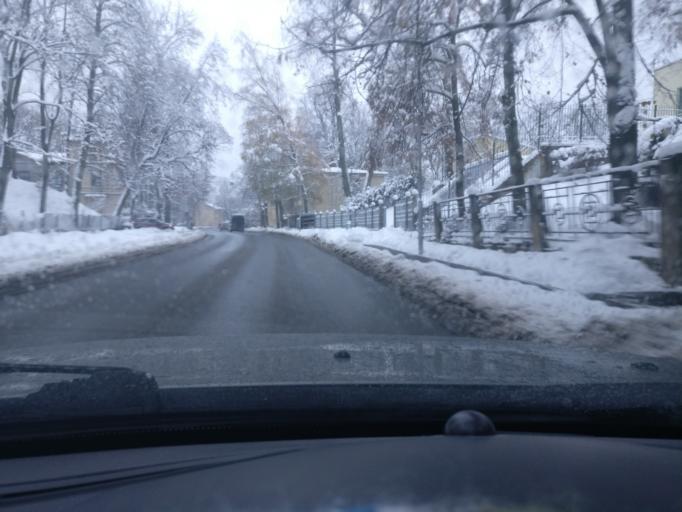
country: LV
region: Riga
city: Riga
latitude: 56.9296
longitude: 24.0811
